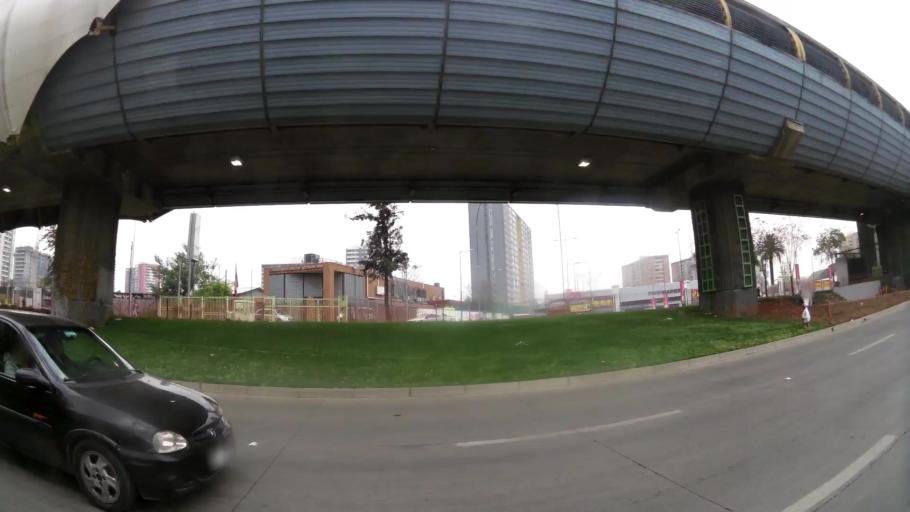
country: CL
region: Santiago Metropolitan
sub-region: Provincia de Santiago
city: Villa Presidente Frei, Nunoa, Santiago, Chile
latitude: -33.5135
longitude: -70.6055
